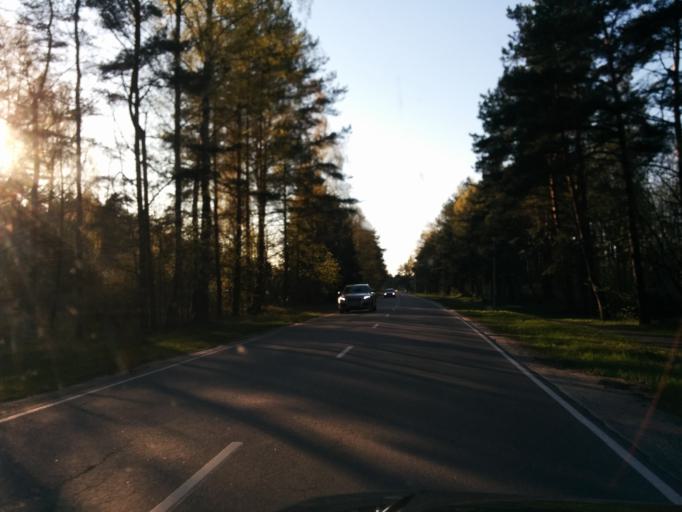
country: LV
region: Engure
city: Smarde
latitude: 57.0151
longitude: 23.5029
